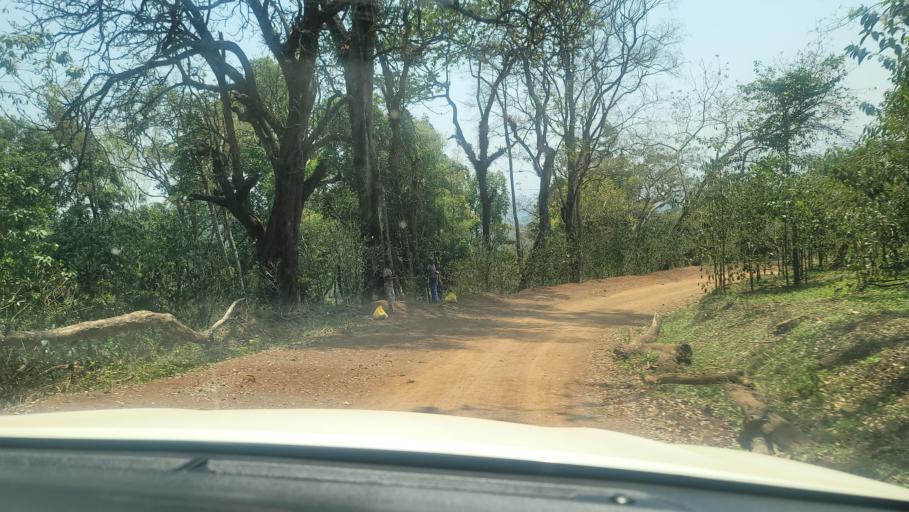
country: ET
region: Southern Nations, Nationalities, and People's Region
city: Bonga
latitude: 7.5371
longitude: 36.1838
